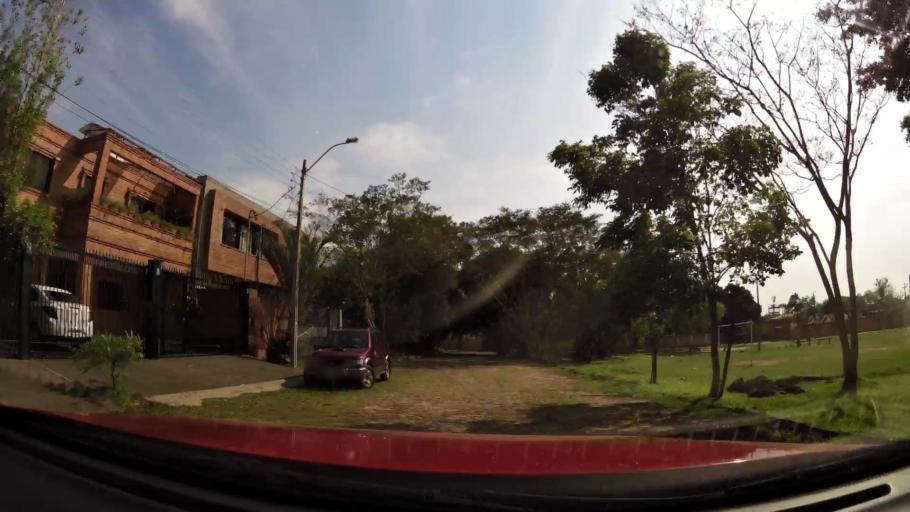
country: PY
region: Central
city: Fernando de la Mora
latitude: -25.2642
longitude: -57.5542
